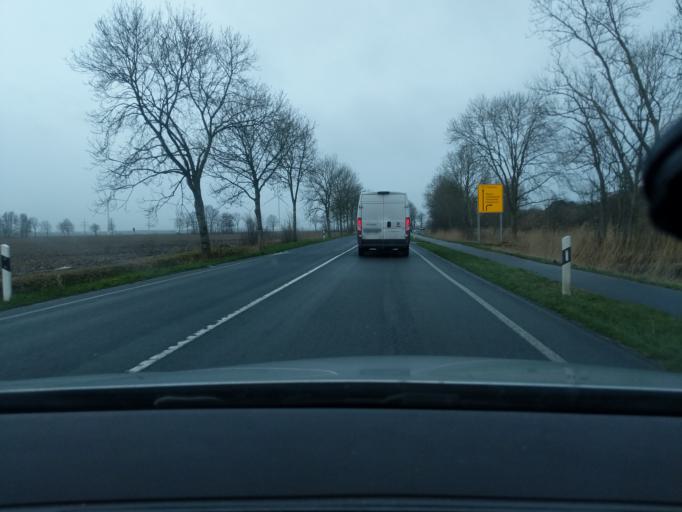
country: DE
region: Lower Saxony
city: Wanna
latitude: 53.8135
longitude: 8.7706
